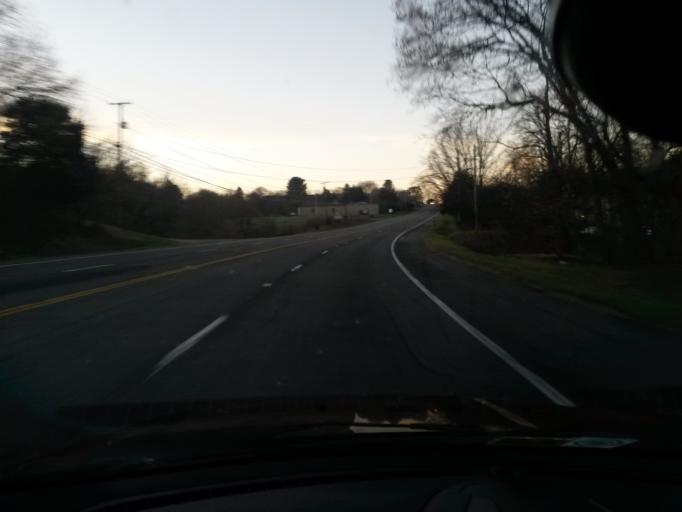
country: US
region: Virginia
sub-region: Botetourt County
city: Fincastle
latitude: 37.5057
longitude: -79.8769
